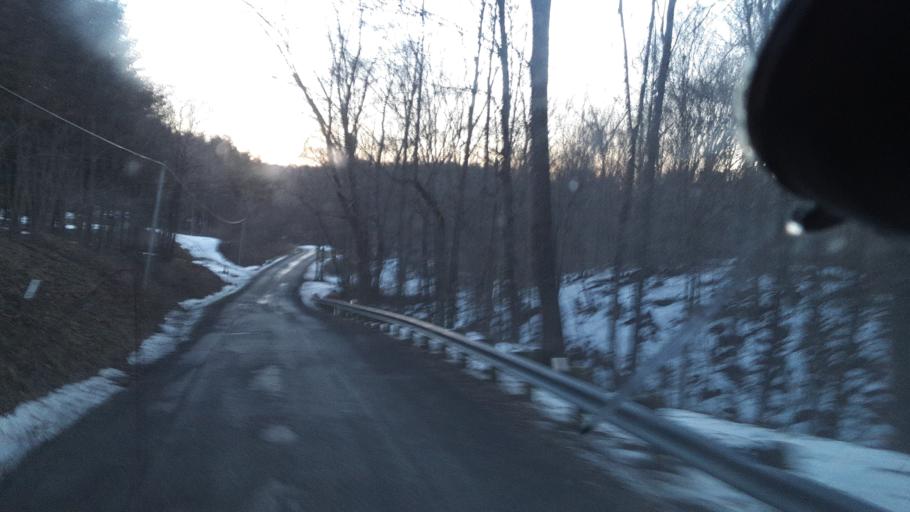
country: US
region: Ohio
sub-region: Perry County
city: Somerset
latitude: 39.7033
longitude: -82.3164
